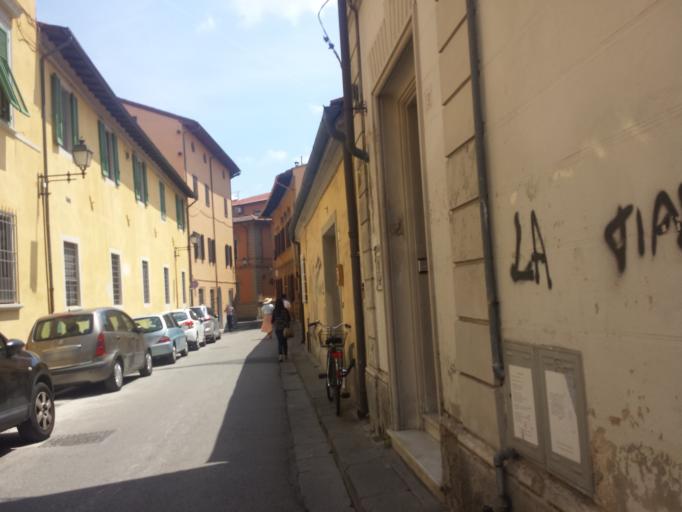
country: IT
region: Tuscany
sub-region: Province of Pisa
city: Pisa
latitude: 43.7218
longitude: 10.3997
